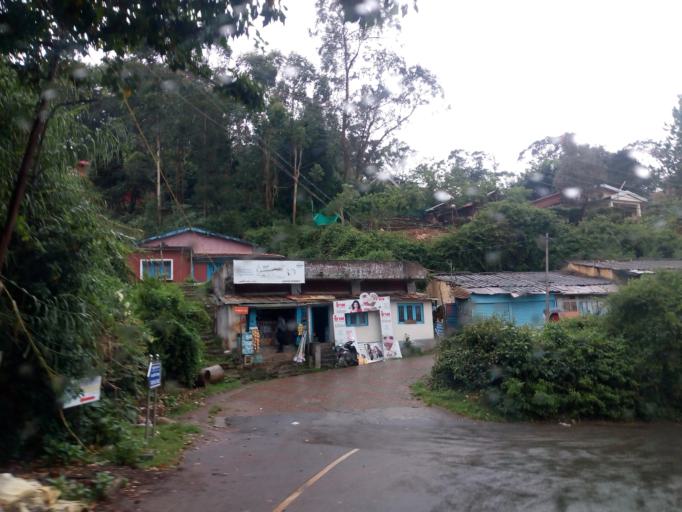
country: IN
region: Tamil Nadu
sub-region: Nilgiri
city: Wellington
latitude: 11.3501
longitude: 76.8079
